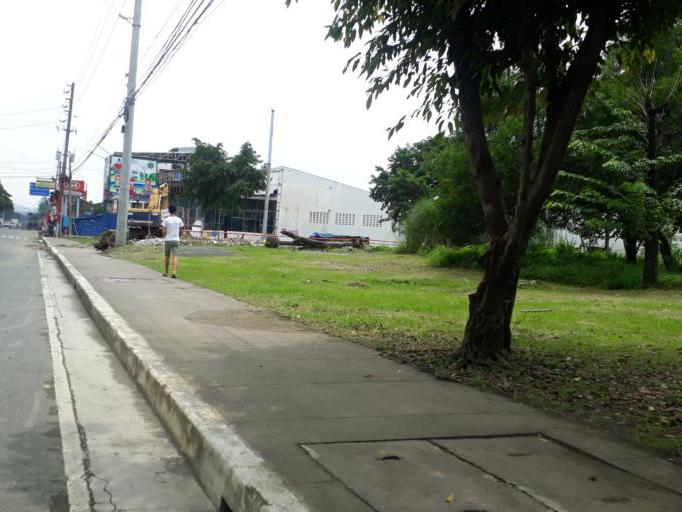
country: PH
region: Calabarzon
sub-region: Province of Rizal
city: Antipolo
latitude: 14.6342
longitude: 121.1056
